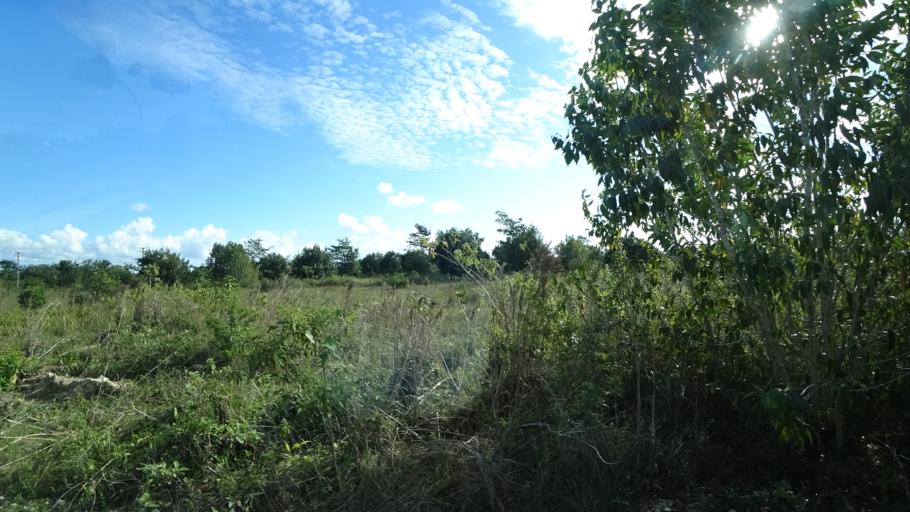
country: BZ
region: Belize
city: Belize City
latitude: 17.5566
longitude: -88.4006
